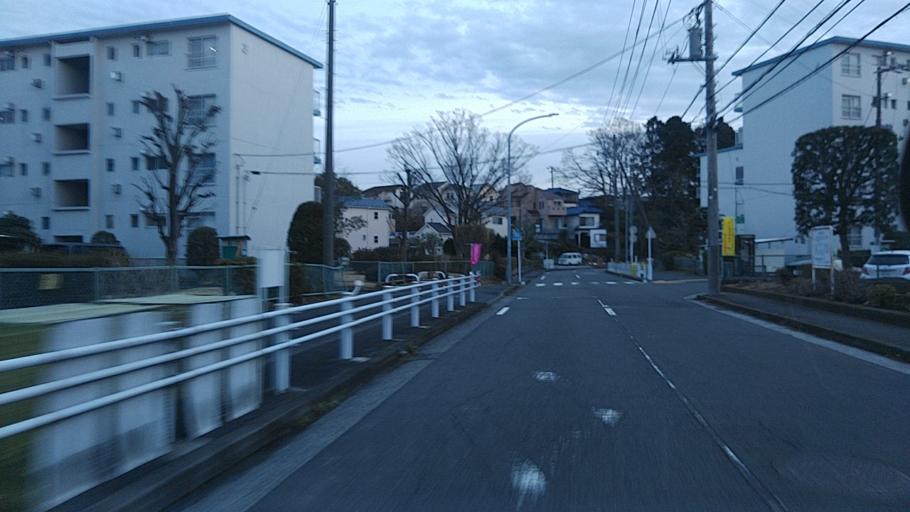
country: JP
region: Kanagawa
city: Fujisawa
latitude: 35.4130
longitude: 139.4920
